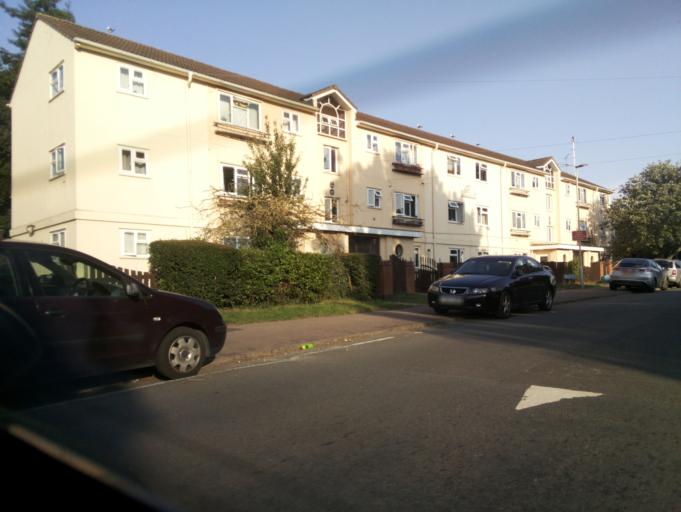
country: GB
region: England
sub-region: Gloucestershire
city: Barnwood
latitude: 51.8386
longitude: -2.2153
